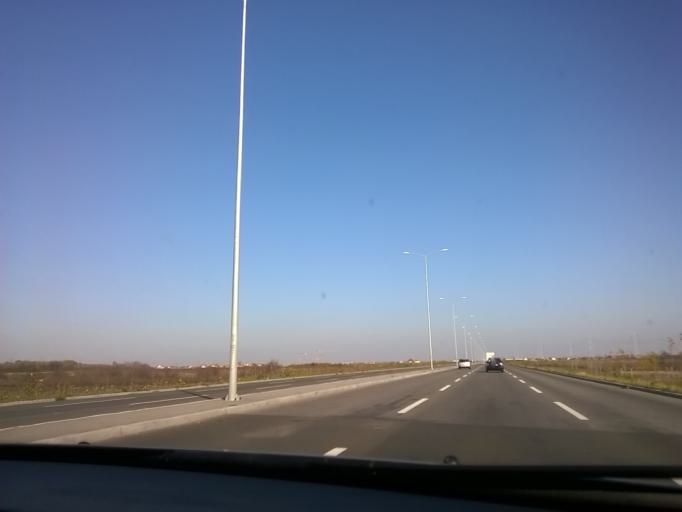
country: RS
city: Ovca
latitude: 44.8698
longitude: 20.5160
